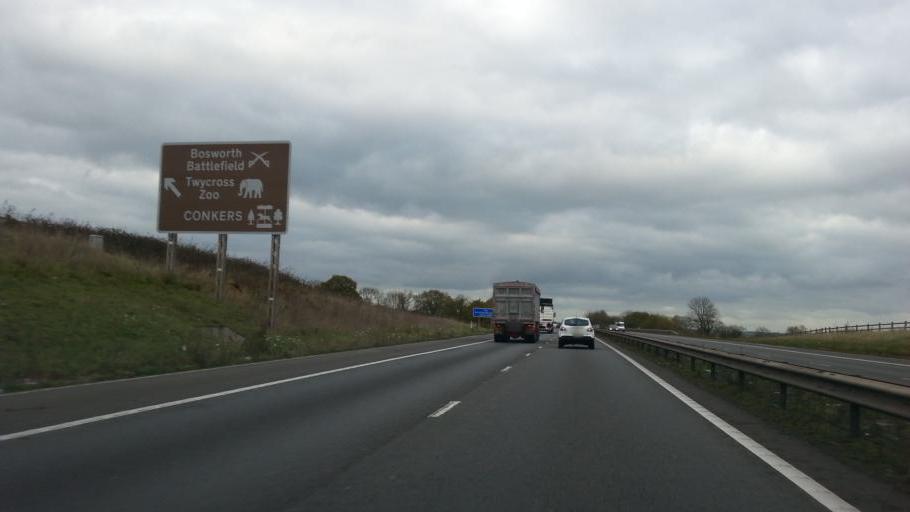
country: GB
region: England
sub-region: Derbyshire
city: Netherseal
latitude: 52.6735
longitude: -1.5594
